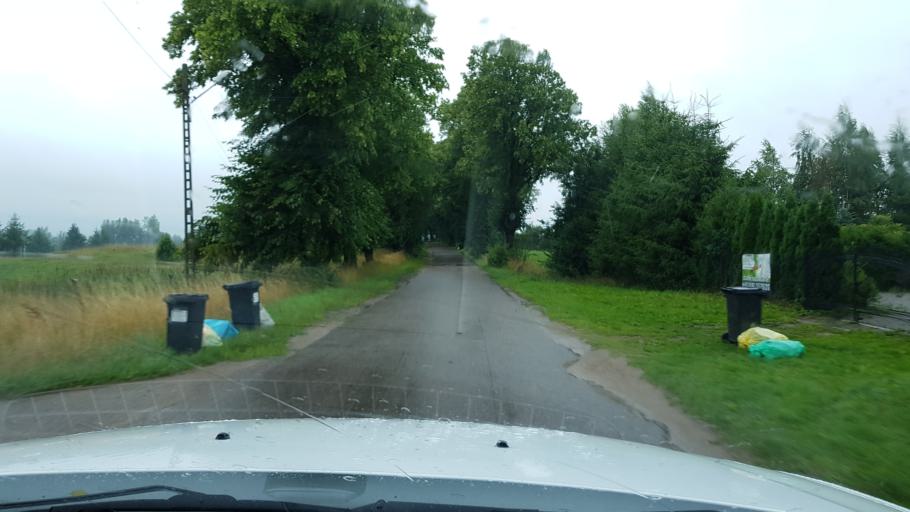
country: PL
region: West Pomeranian Voivodeship
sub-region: Powiat kolobrzeski
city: Ustronie Morskie
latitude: 54.2136
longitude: 15.8767
